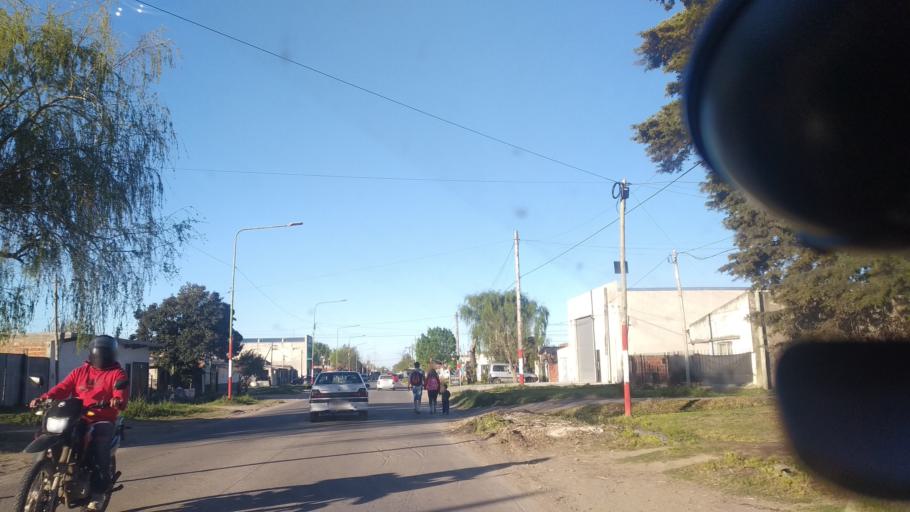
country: AR
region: Buenos Aires
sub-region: Partido de La Plata
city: La Plata
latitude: -34.9639
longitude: -57.9640
